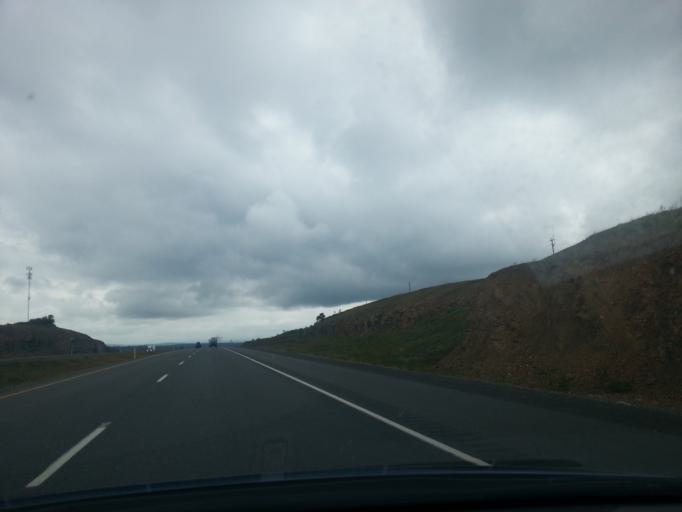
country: US
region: Maine
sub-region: Aroostook County
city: Limestone
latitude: 46.9331
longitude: -67.7374
